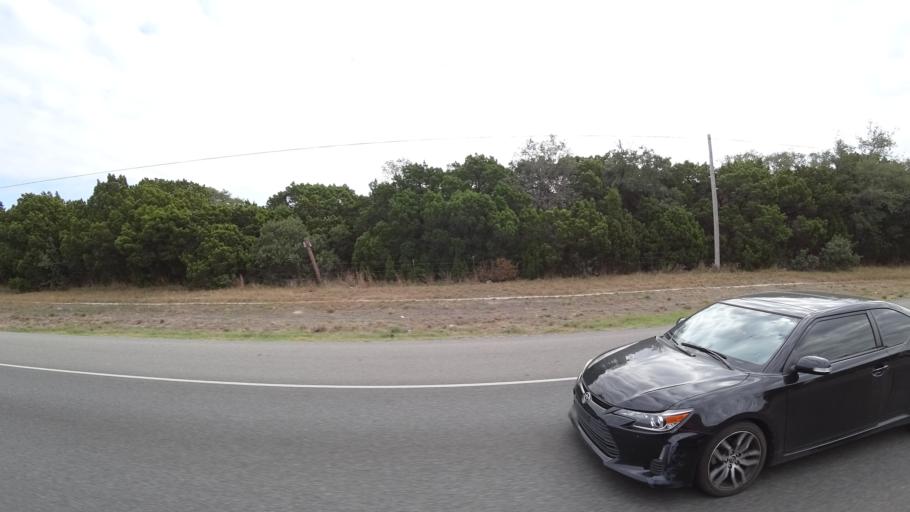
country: US
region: Texas
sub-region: Williamson County
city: Anderson Mill
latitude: 30.4246
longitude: -97.8441
